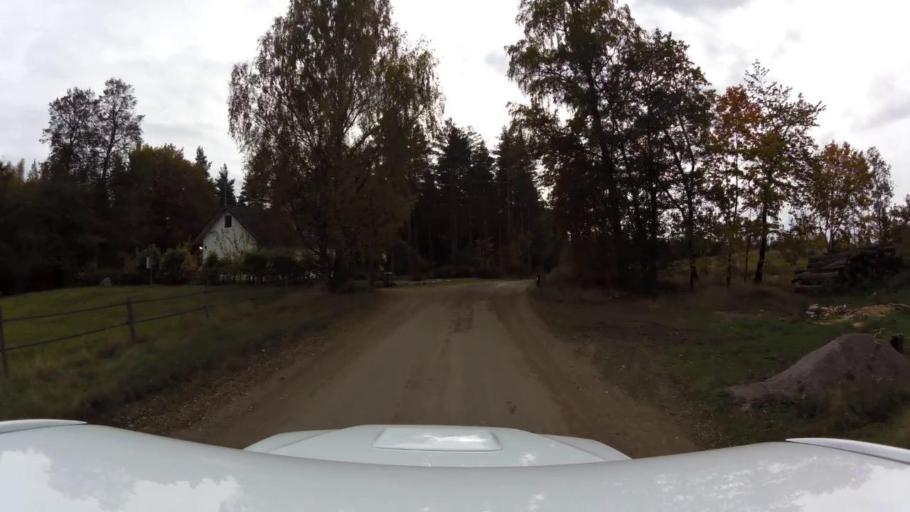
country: SE
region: OEstergoetland
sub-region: Linkopings Kommun
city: Ekangen
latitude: 58.5552
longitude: 15.6636
